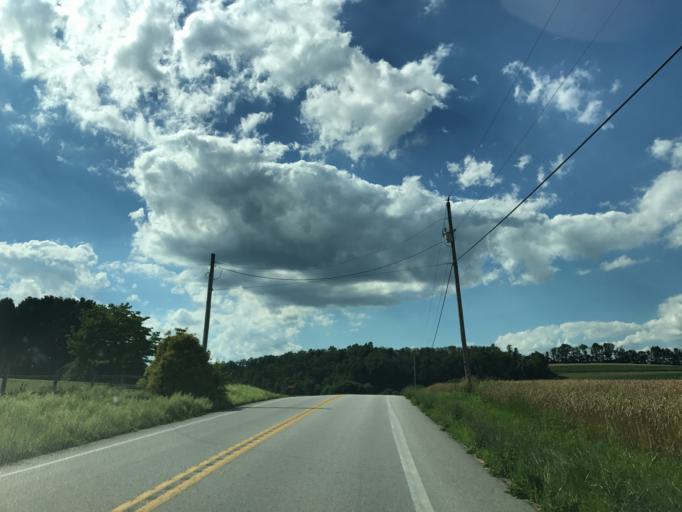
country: US
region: Pennsylvania
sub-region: York County
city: Glen Rock
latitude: 39.7375
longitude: -76.7791
